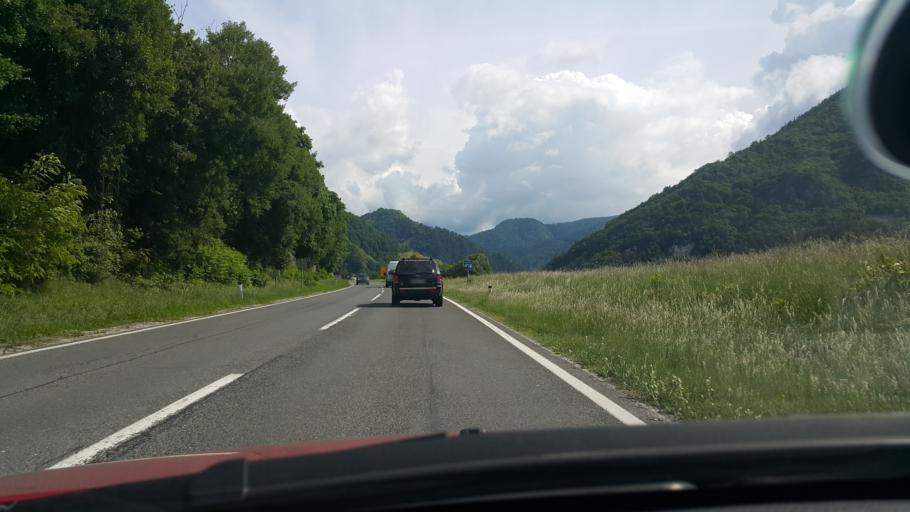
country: SI
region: Trzic
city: Bistrica pri Trzicu
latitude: 46.3503
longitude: 14.2900
